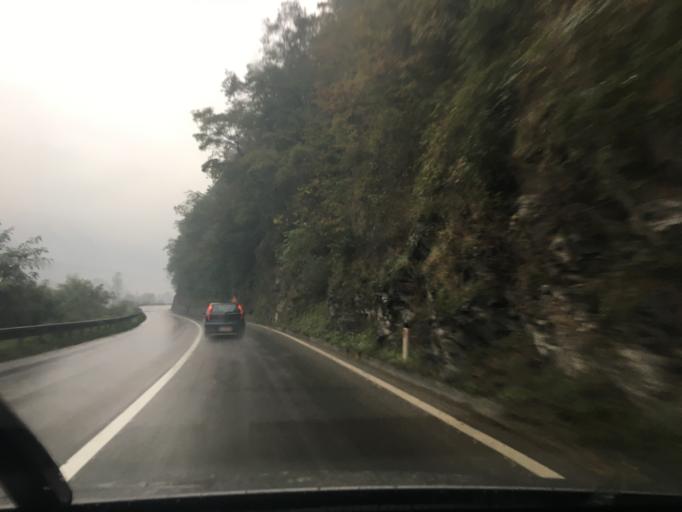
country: RS
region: Central Serbia
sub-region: Pcinjski Okrug
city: Vladicin Han
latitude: 42.7950
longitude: 22.0967
